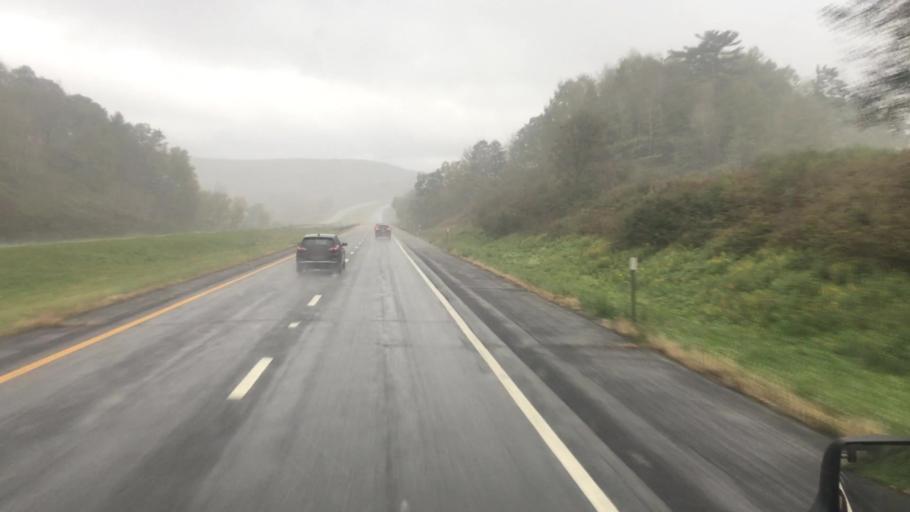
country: US
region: New York
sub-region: Chenango County
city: Bainbridge
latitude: 42.1846
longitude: -75.6065
